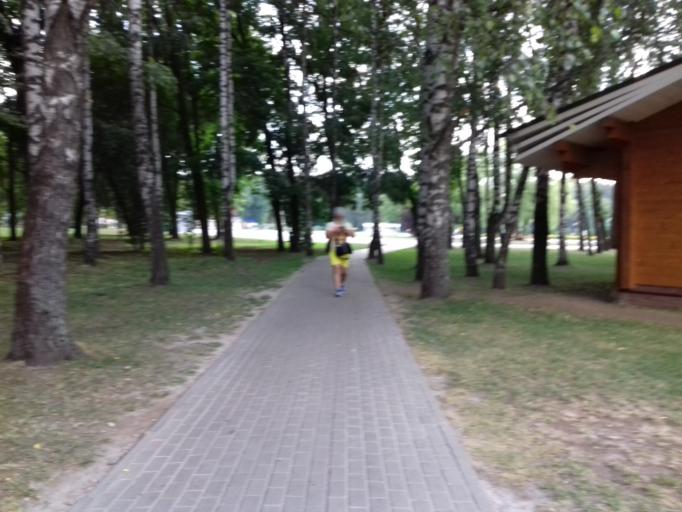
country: RU
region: Tula
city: Tula
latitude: 54.1806
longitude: 37.5874
